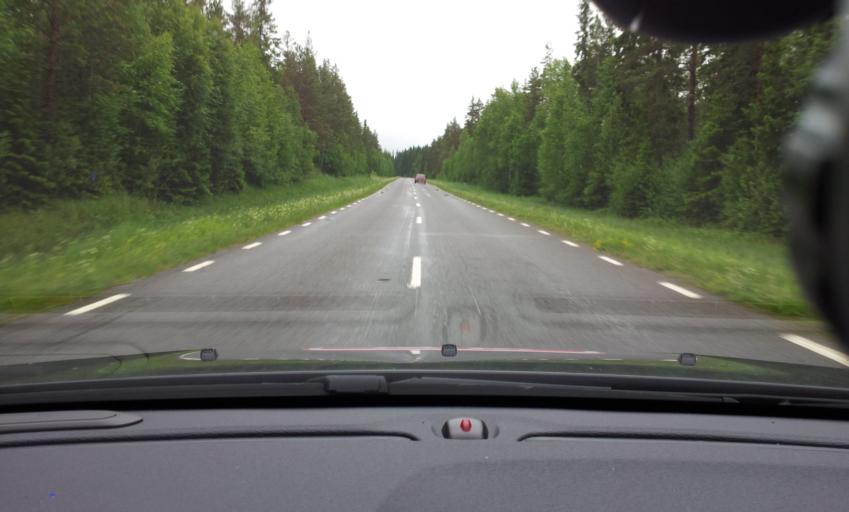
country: SE
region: Jaemtland
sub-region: Stroemsunds Kommun
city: Stroemsund
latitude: 63.4758
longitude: 15.4458
